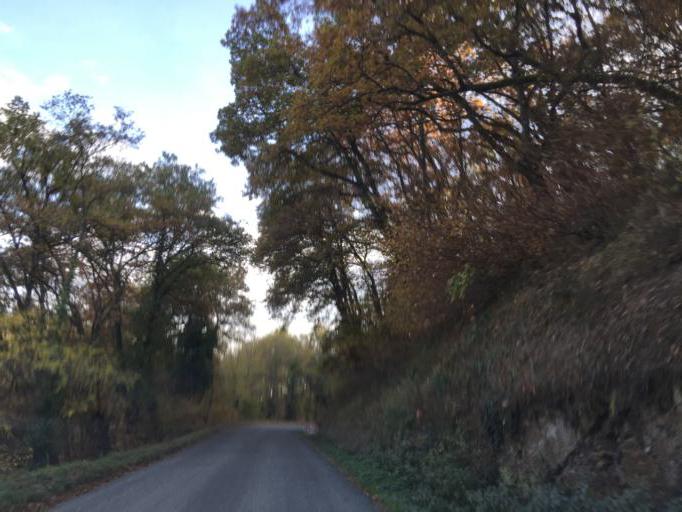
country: FR
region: Rhone-Alpes
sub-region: Departement de la Loire
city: Lorette
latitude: 45.5301
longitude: 4.5713
